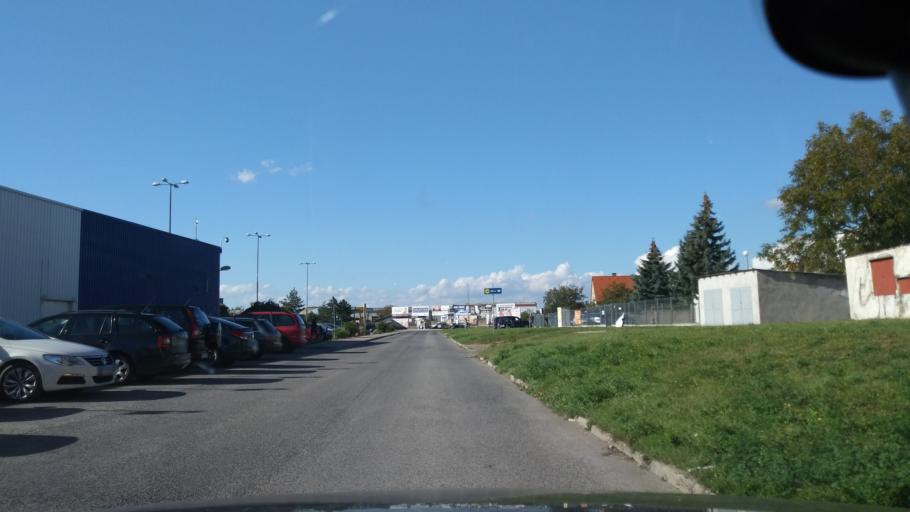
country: SK
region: Trnavsky
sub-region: Okres Skalica
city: Skalica
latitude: 48.8399
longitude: 17.2196
